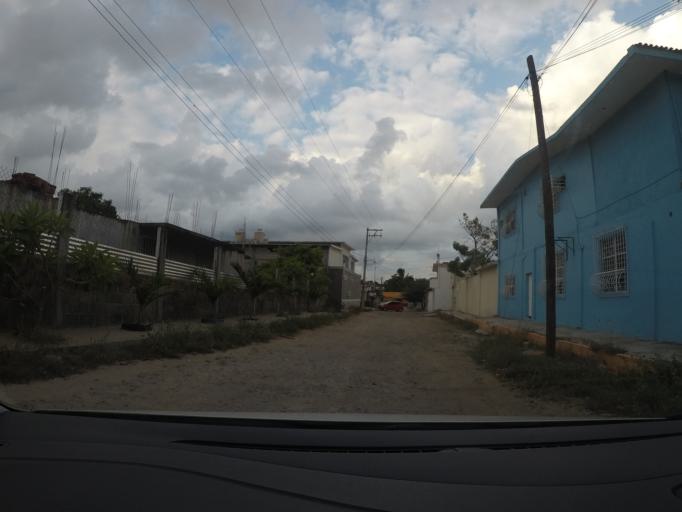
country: MX
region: Oaxaca
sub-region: Salina Cruz
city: Salina Cruz
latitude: 16.2067
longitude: -95.1978
